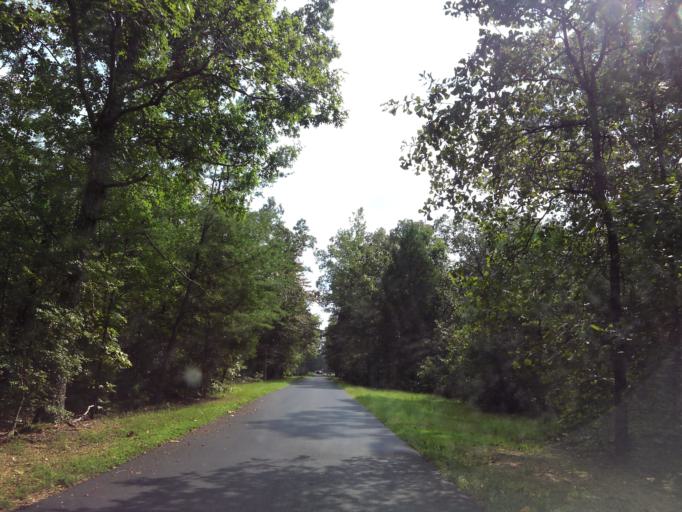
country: US
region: Tennessee
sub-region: Hardin County
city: Crump
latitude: 35.1422
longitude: -88.3490
